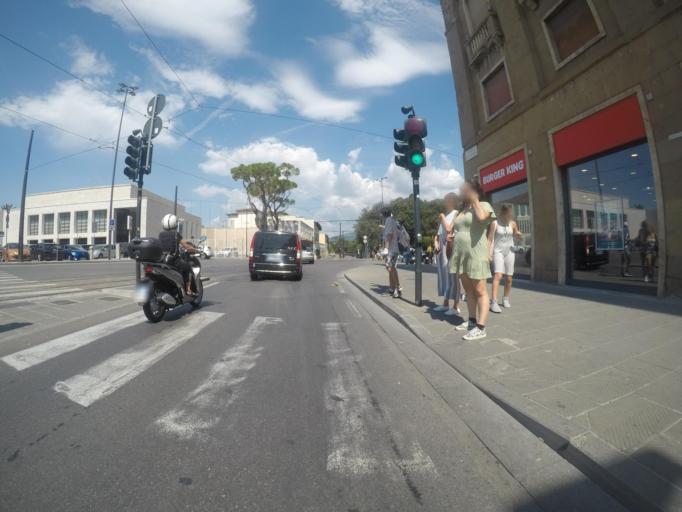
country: IT
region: Tuscany
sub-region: Province of Florence
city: Florence
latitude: 43.7769
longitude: 11.2494
